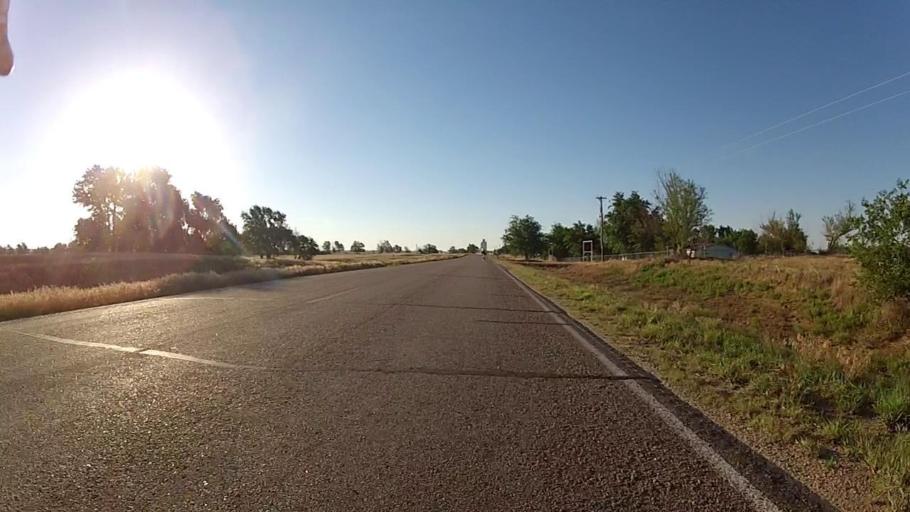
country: US
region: Kansas
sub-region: Ford County
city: Dodge City
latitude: 37.7081
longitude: -99.9110
